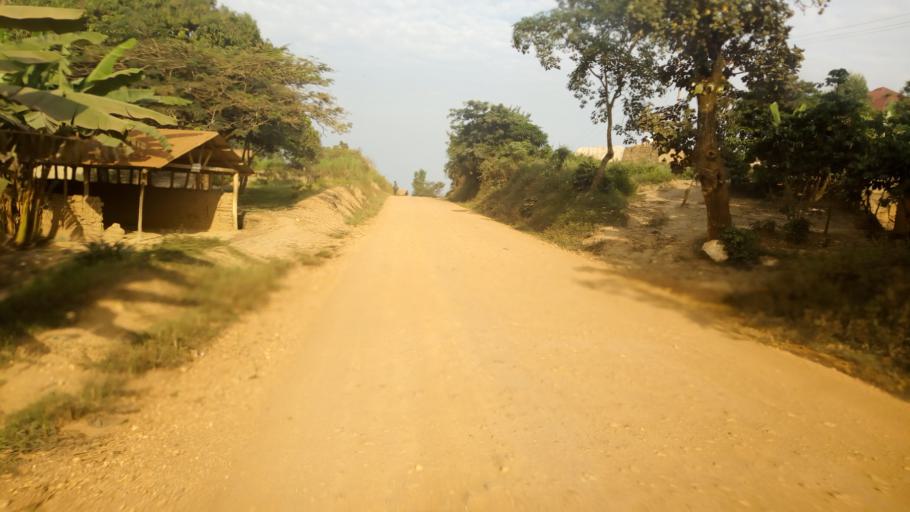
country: UG
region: Western Region
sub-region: Kanungu District
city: Ntungamo
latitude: -0.8350
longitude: 29.6753
